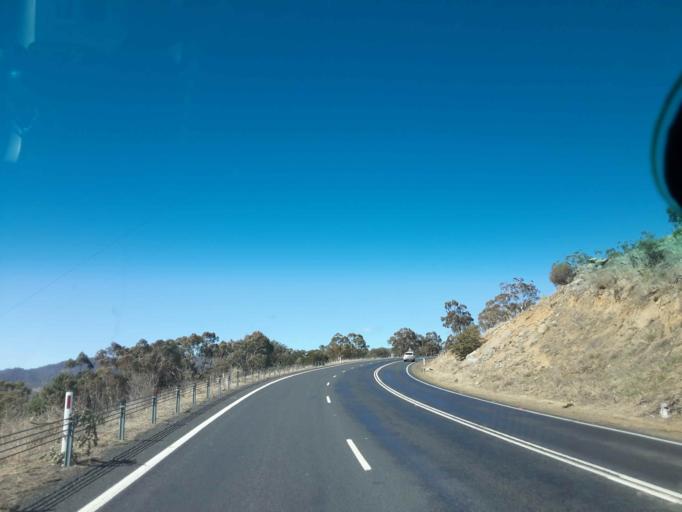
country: AU
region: New South Wales
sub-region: Snowy River
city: Jindabyne
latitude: -36.4122
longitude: 148.6029
